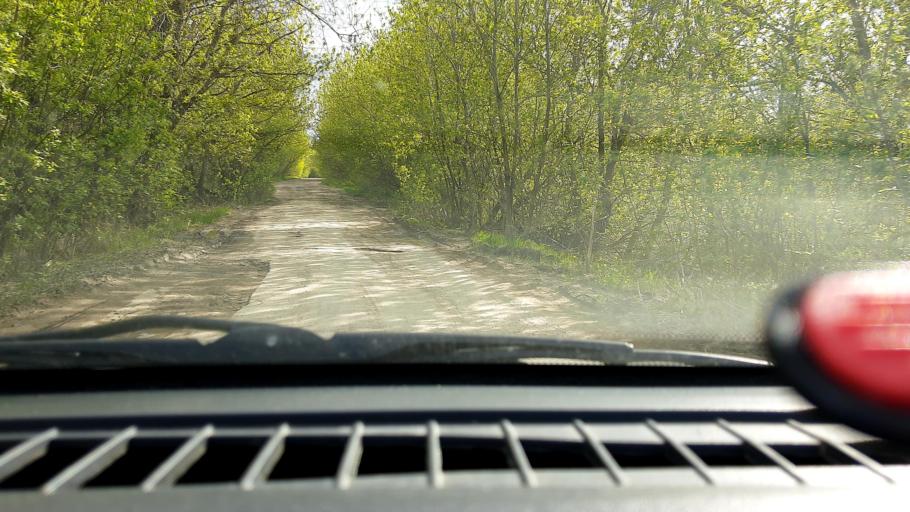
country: RU
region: Nizjnij Novgorod
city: Neklyudovo
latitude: 56.3947
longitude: 43.8477
